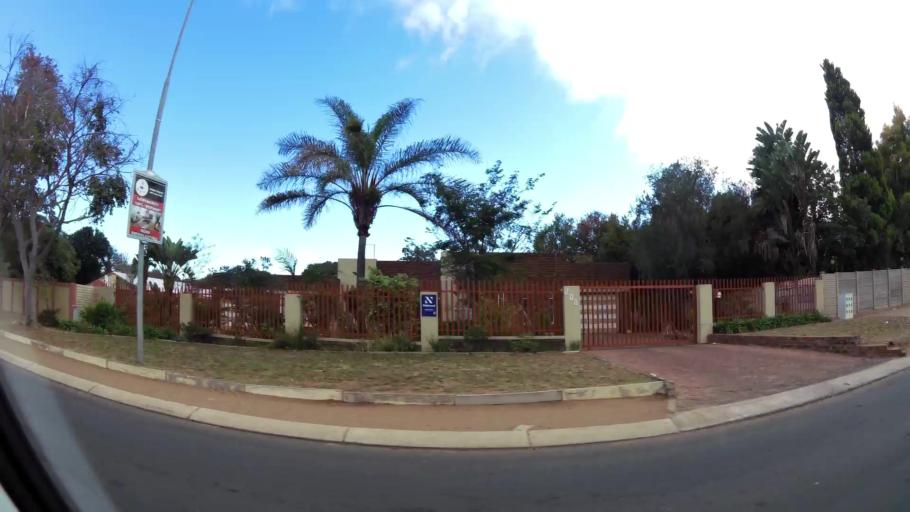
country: ZA
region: Limpopo
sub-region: Capricorn District Municipality
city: Polokwane
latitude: -23.9165
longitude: 29.4739
